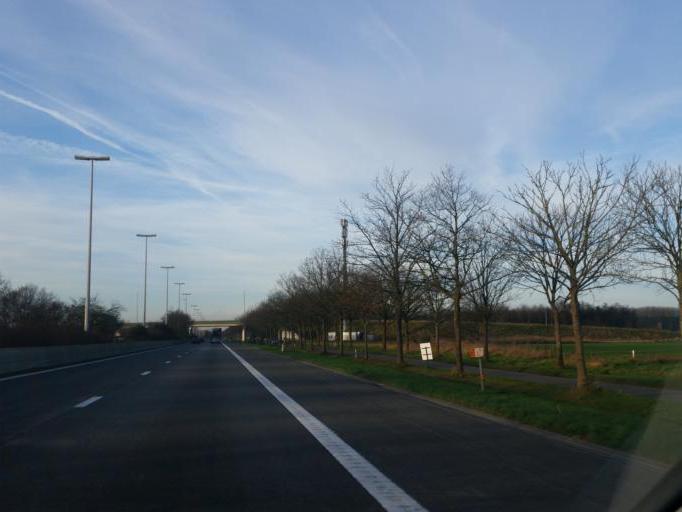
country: BE
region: Flanders
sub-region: Provincie Oost-Vlaanderen
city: Wachtebeke
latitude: 51.1887
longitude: 3.8882
